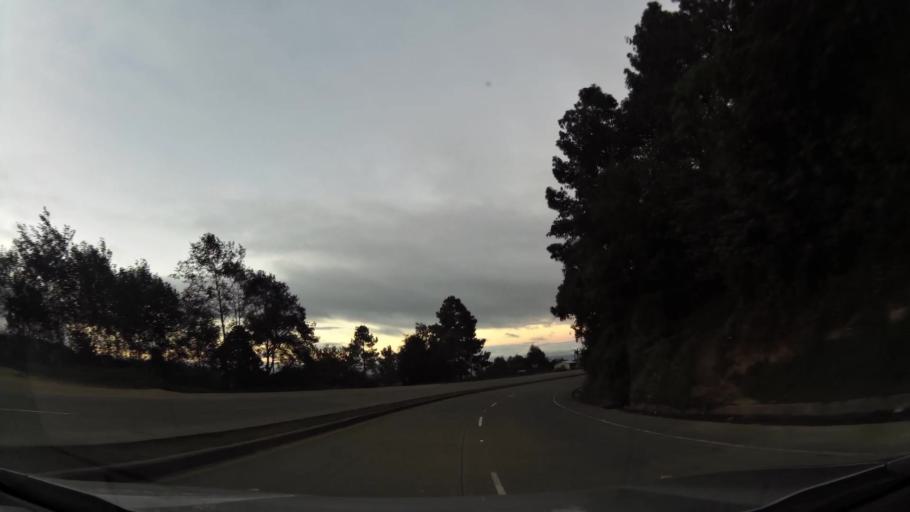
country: GT
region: Solola
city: Concepcion
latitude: 14.8309
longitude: -91.0802
